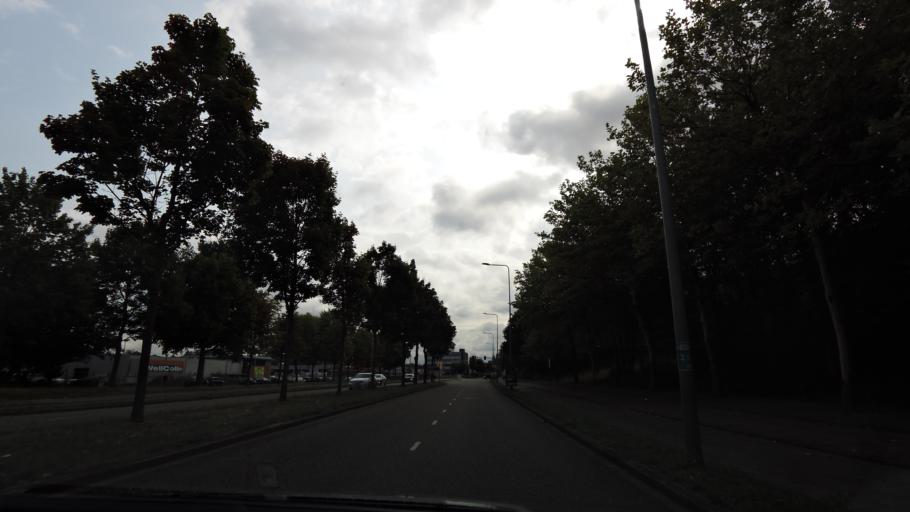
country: NL
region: Limburg
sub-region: Gemeente Heerlen
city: Nieuw-Lotbroek
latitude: 50.9040
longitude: 5.9559
